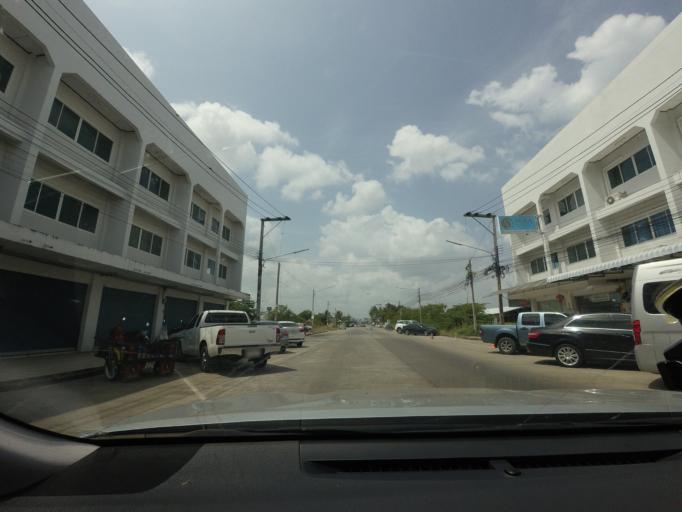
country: TH
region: Nakhon Si Thammarat
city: Nakhon Si Thammarat
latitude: 8.4285
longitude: 99.9796
